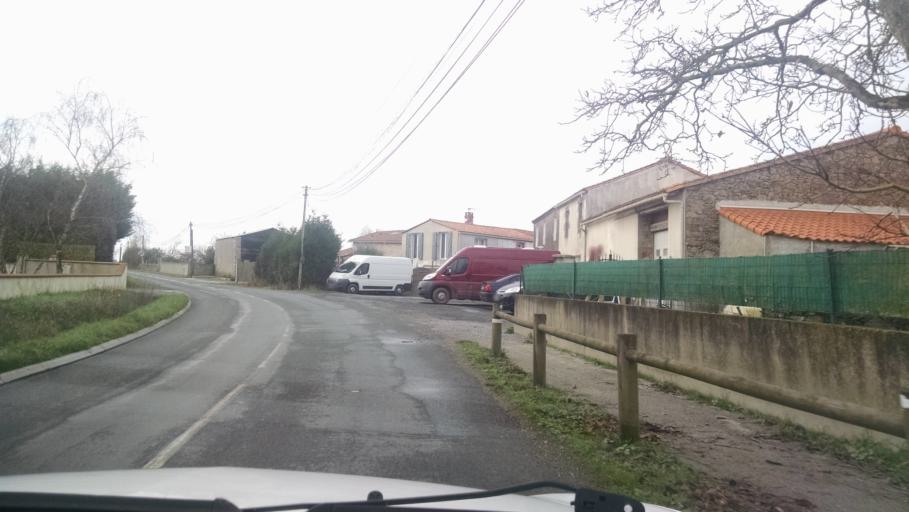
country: FR
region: Pays de la Loire
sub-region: Departement de la Loire-Atlantique
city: Saint-Hilaire-de-Clisson
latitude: 47.0624
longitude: -1.3204
